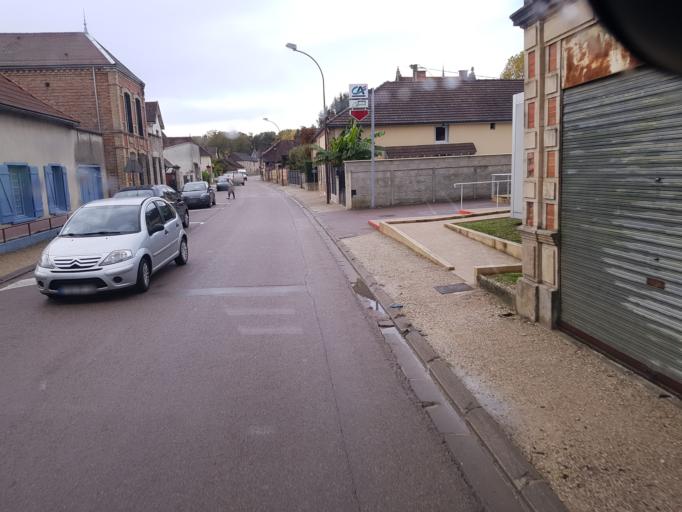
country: FR
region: Champagne-Ardenne
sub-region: Departement de l'Aube
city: Lusigny-sur-Barse
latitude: 48.2538
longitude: 4.2653
